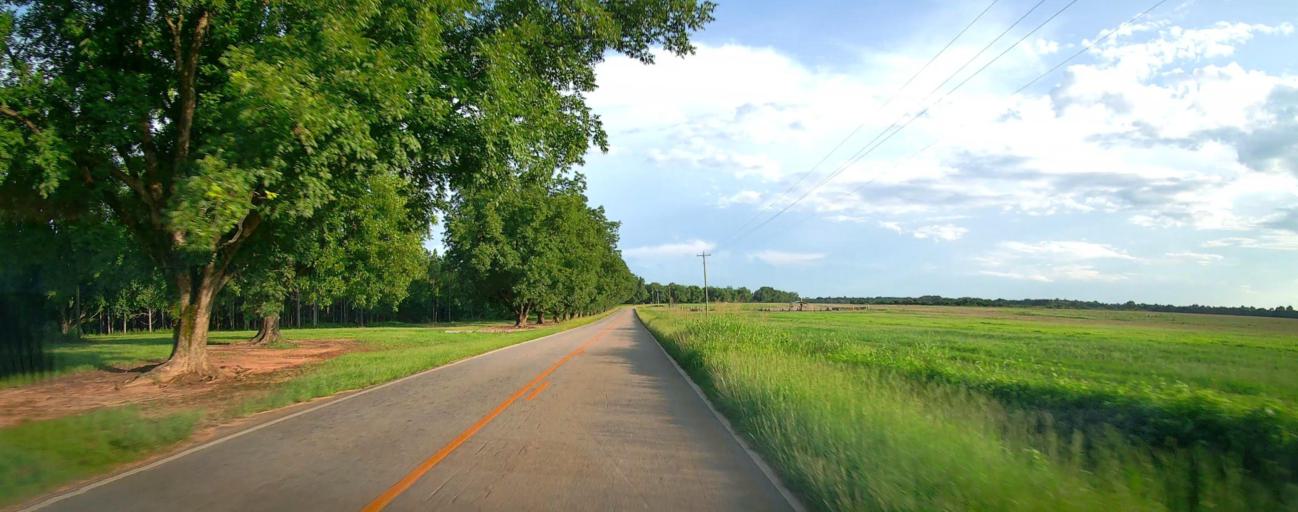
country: US
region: Georgia
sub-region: Peach County
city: Byron
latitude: 32.6574
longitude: -83.8608
